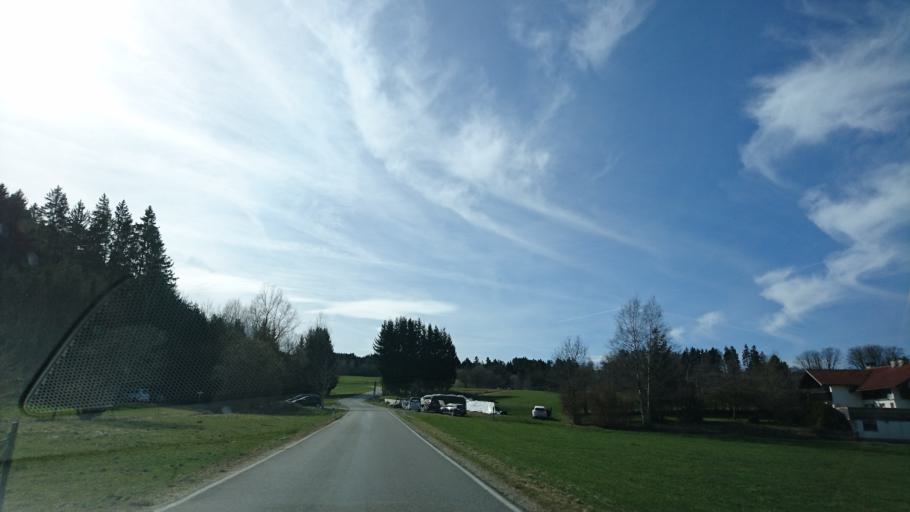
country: DE
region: Bavaria
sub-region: Upper Bavaria
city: Bernbeuren
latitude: 47.7372
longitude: 10.7705
